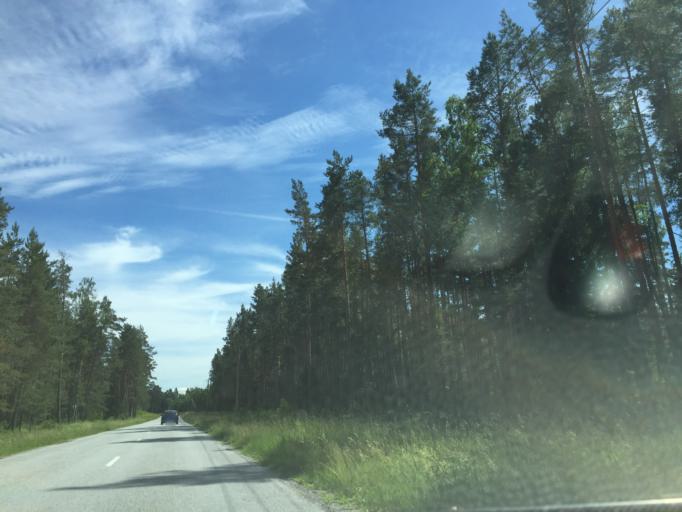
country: LV
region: Talsu Rajons
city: Valdemarpils
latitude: 57.5930
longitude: 22.6077
